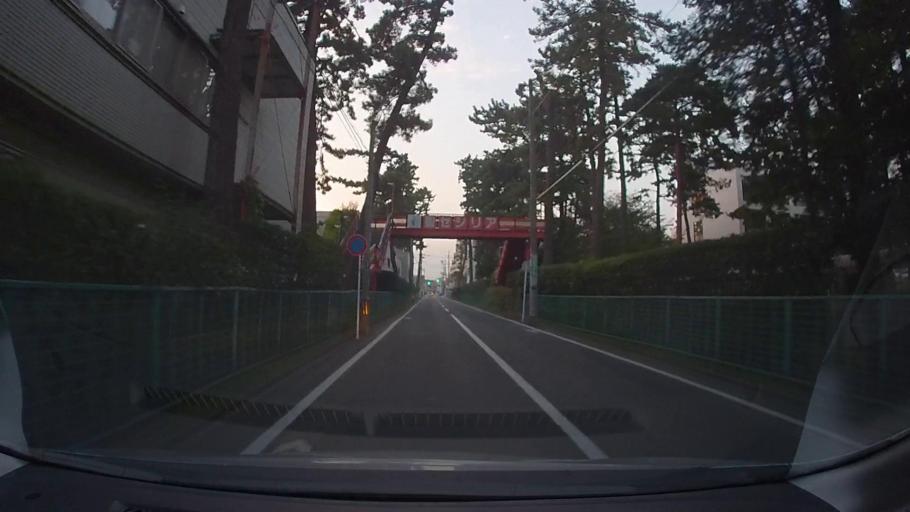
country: JP
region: Kanagawa
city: Minami-rinkan
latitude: 35.4993
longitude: 139.4447
